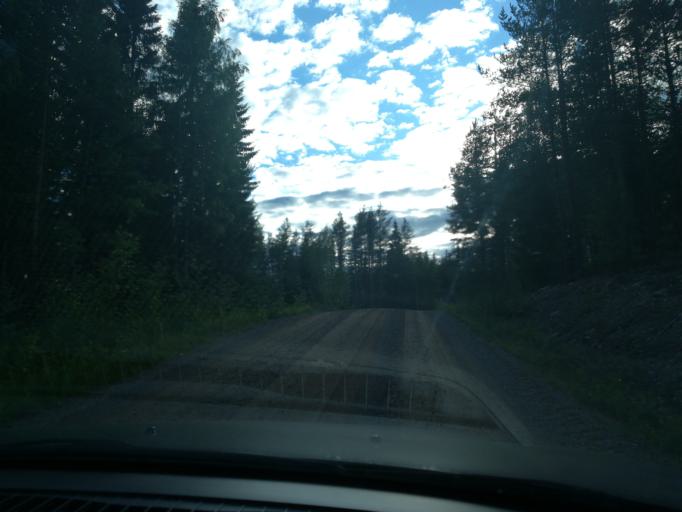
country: FI
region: Southern Savonia
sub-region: Mikkeli
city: Puumala
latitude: 61.5929
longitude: 28.1536
